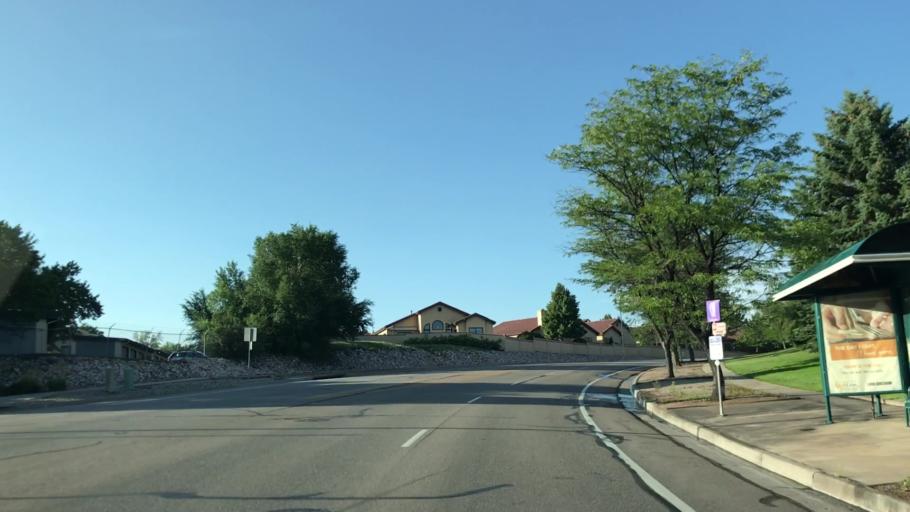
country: US
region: Colorado
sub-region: El Paso County
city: Colorado Springs
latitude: 38.8665
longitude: -104.8636
